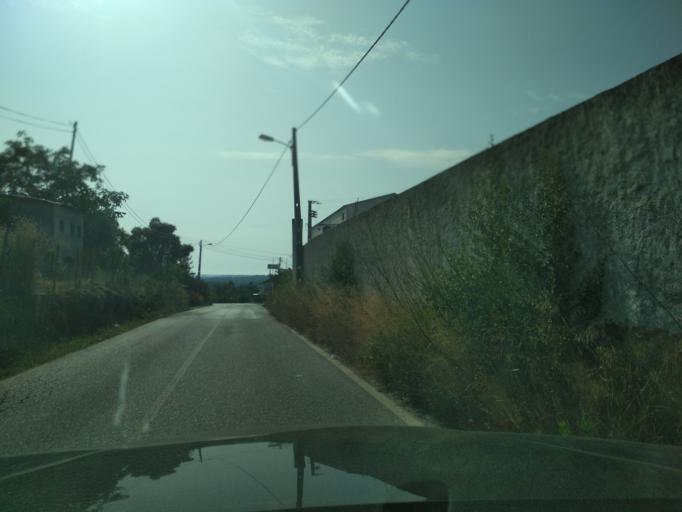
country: PT
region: Coimbra
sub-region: Condeixa-A-Nova
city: Condeixa-a-Nova
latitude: 40.1457
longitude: -8.4611
